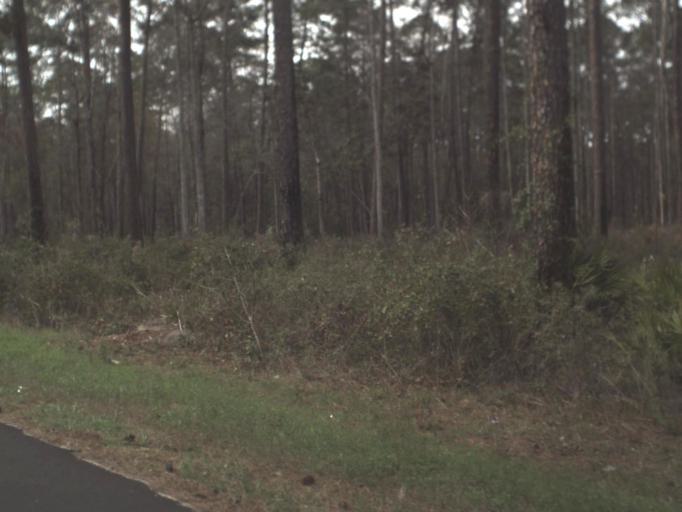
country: US
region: Florida
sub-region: Gadsden County
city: Quincy
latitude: 30.3884
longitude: -84.6325
